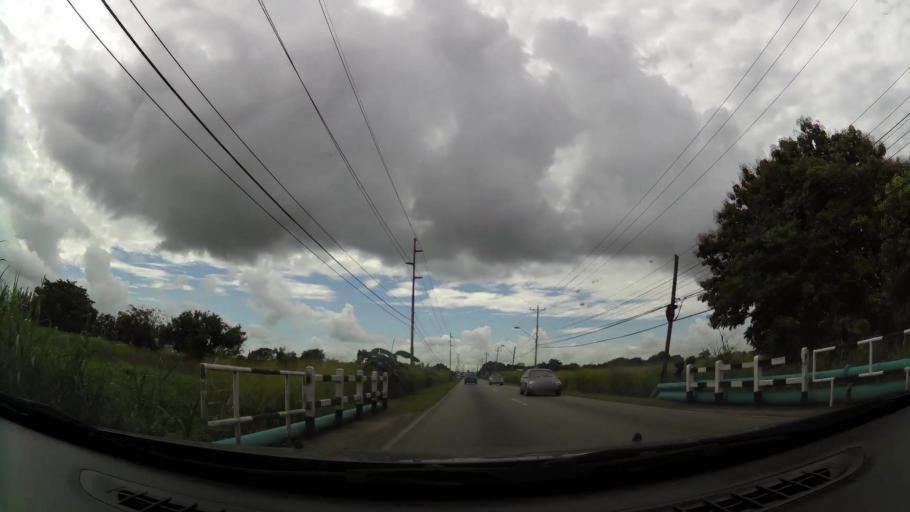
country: TT
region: Chaguanas
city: Chaguanas
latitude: 10.4933
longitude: -61.4081
